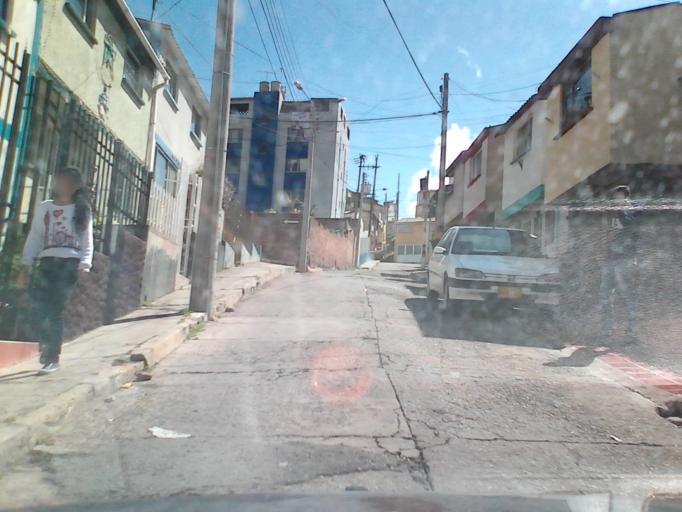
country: CO
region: Boyaca
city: Duitama
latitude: 5.8276
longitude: -73.0394
